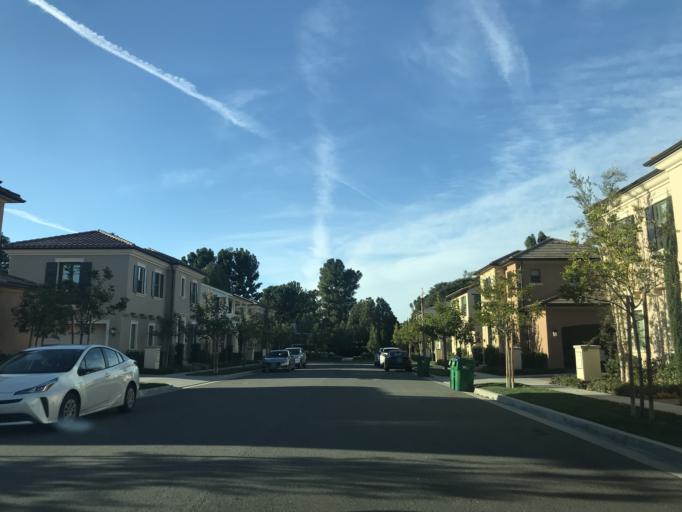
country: US
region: California
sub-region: Orange County
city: North Tustin
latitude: 33.7139
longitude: -117.7545
